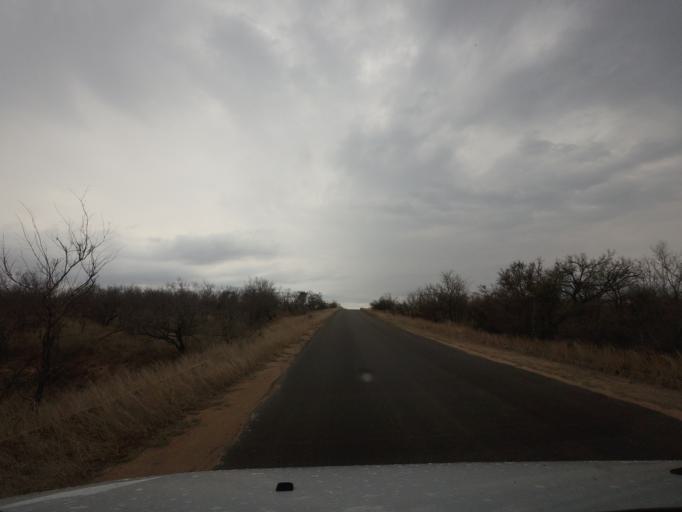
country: ZA
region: Limpopo
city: Thulamahashi
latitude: -24.4689
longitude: 31.4382
